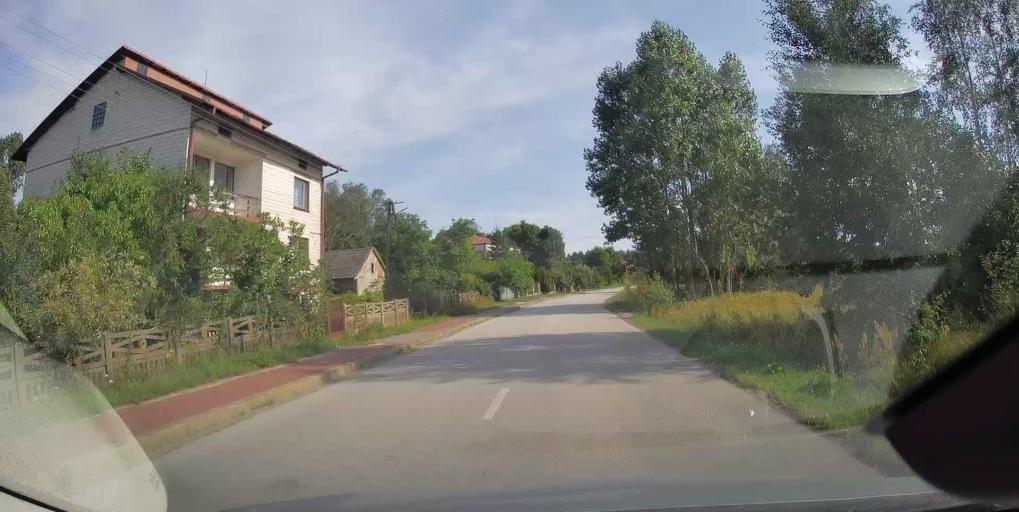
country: PL
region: Lodz Voivodeship
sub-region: Powiat opoczynski
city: Mniszkow
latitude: 51.3437
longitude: 20.0393
